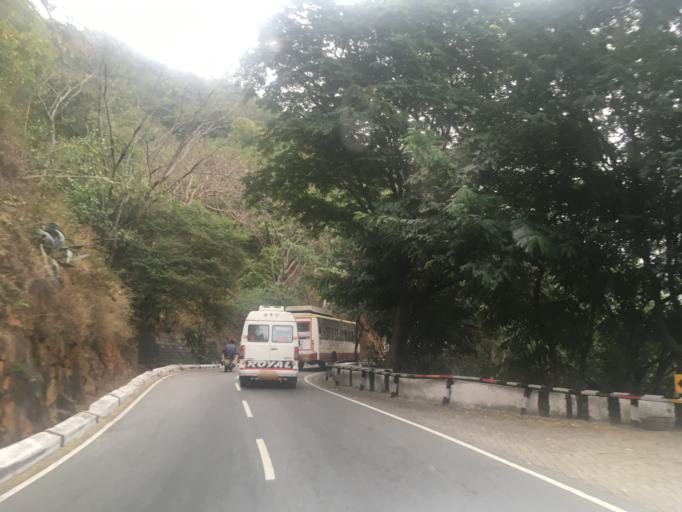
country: IN
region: Andhra Pradesh
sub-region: Chittoor
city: Tirumala
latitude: 13.6664
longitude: 79.3464
